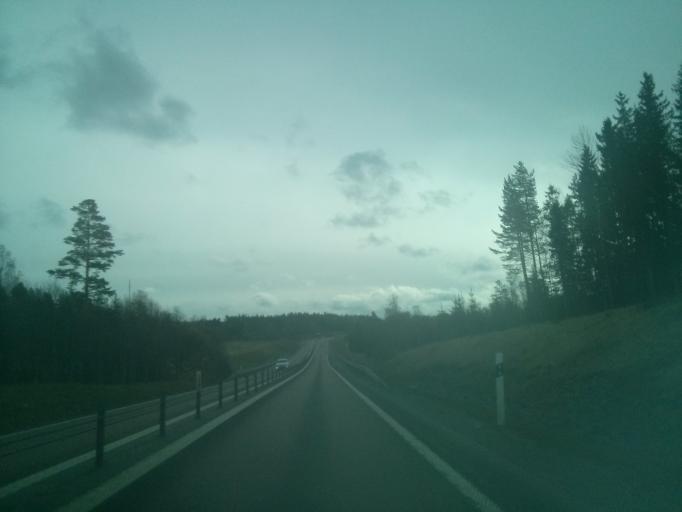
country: SE
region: Vaesternorrland
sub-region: Timra Kommun
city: Soraker
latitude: 62.5418
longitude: 17.5698
